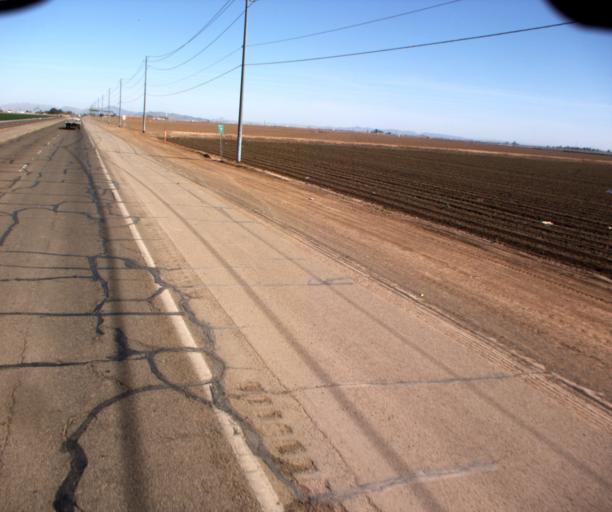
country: US
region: Arizona
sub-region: Yuma County
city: Somerton
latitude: 32.5735
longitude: -114.7698
